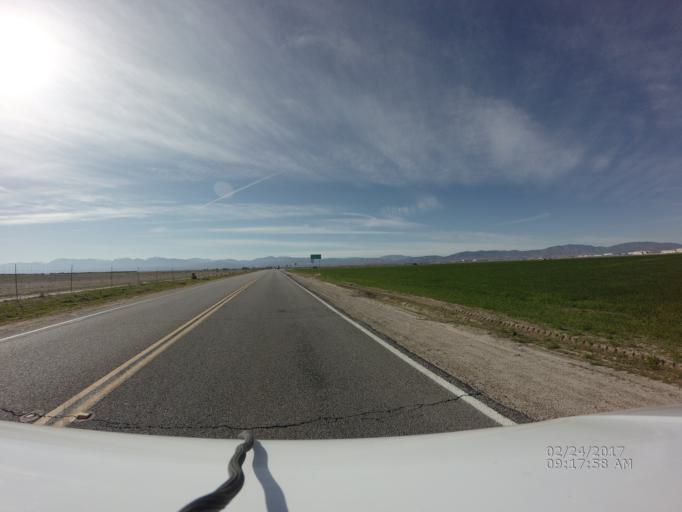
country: US
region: California
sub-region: Los Angeles County
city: Palmdale
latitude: 34.6482
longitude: -118.0410
